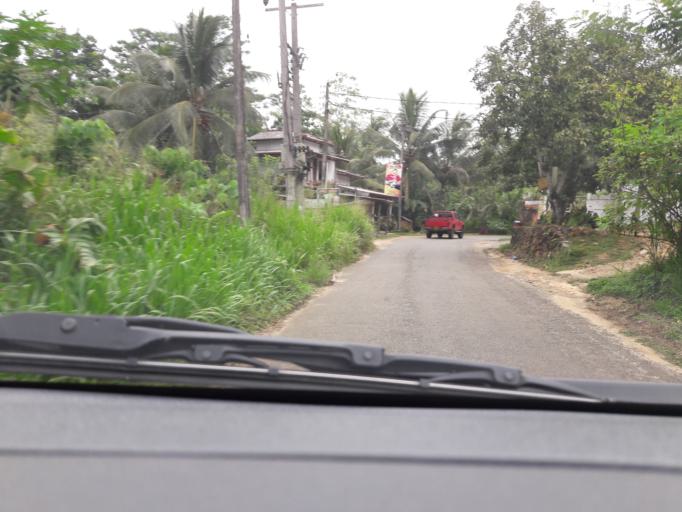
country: LK
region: Southern
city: Galle
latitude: 6.1955
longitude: 80.3020
